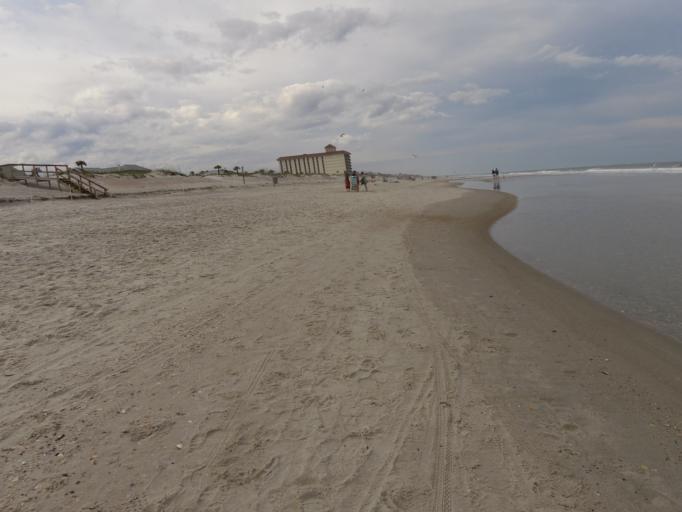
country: US
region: Florida
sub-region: Duval County
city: Neptune Beach
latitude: 30.3215
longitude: -81.3937
